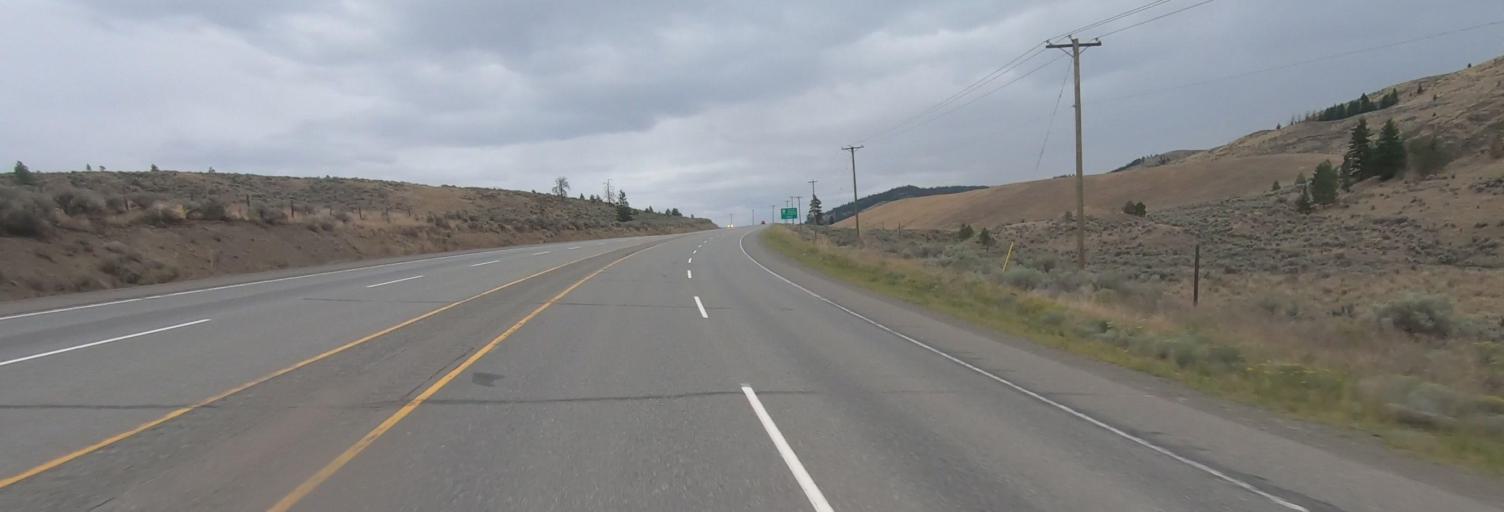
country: CA
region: British Columbia
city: Kamloops
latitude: 50.6701
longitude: -120.4827
